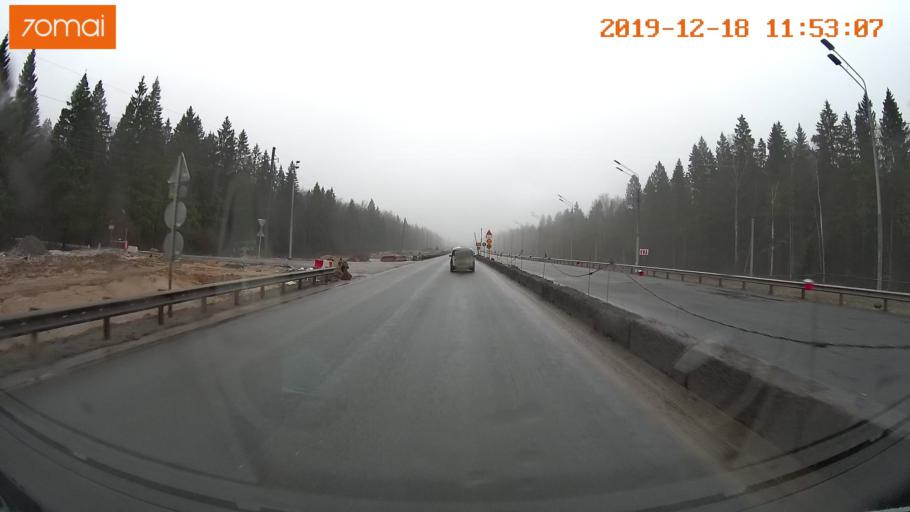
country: RU
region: Moskovskaya
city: Yershovo
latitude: 55.8011
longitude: 36.9206
